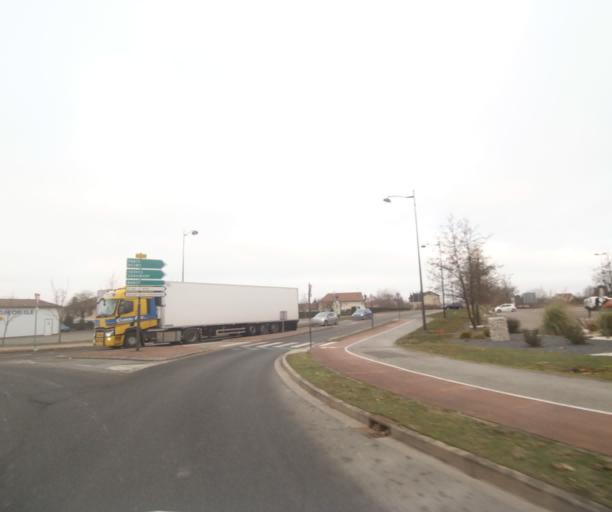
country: FR
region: Champagne-Ardenne
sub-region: Departement de la Haute-Marne
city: Bettancourt-la-Ferree
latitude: 48.6479
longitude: 4.9571
